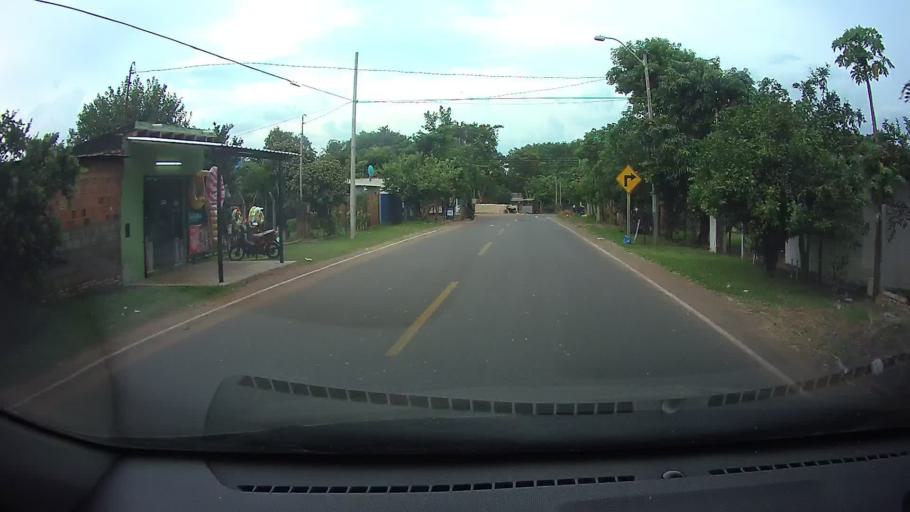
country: PY
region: Central
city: San Lorenzo
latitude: -25.2743
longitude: -57.4675
